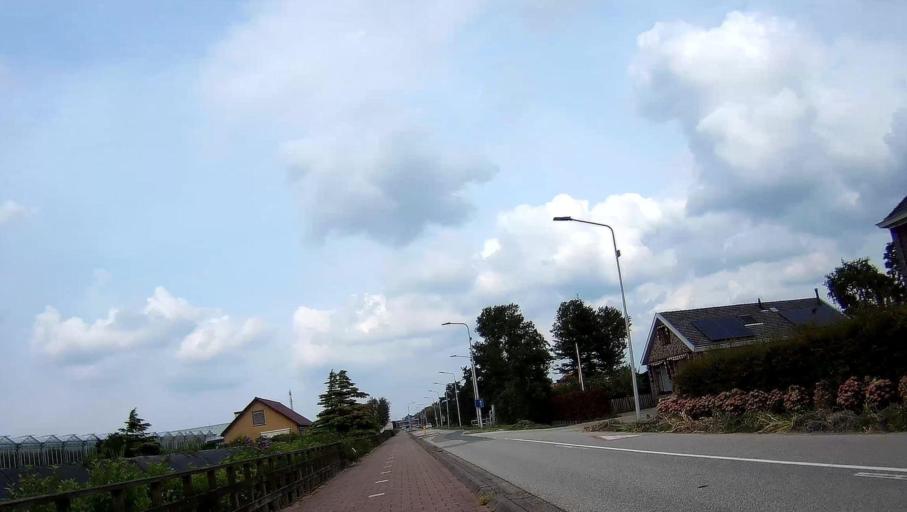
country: NL
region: South Holland
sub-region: Gemeente Westland
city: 's-Gravenzande
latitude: 51.9849
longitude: 4.1831
